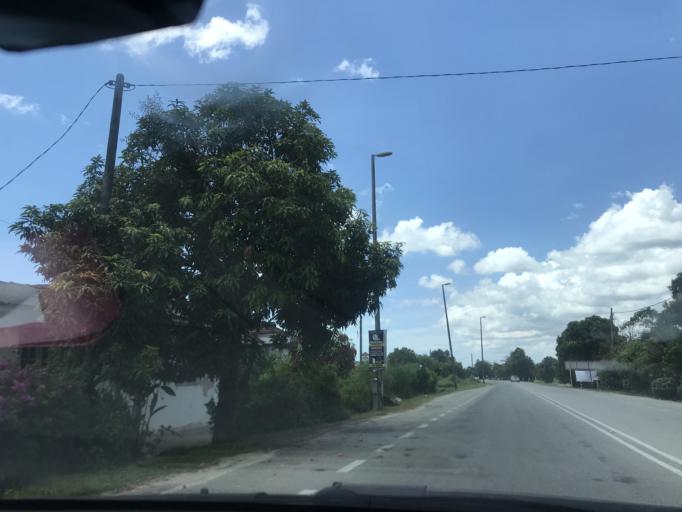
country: MY
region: Kelantan
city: Tumpat
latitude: 6.2087
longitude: 102.1106
